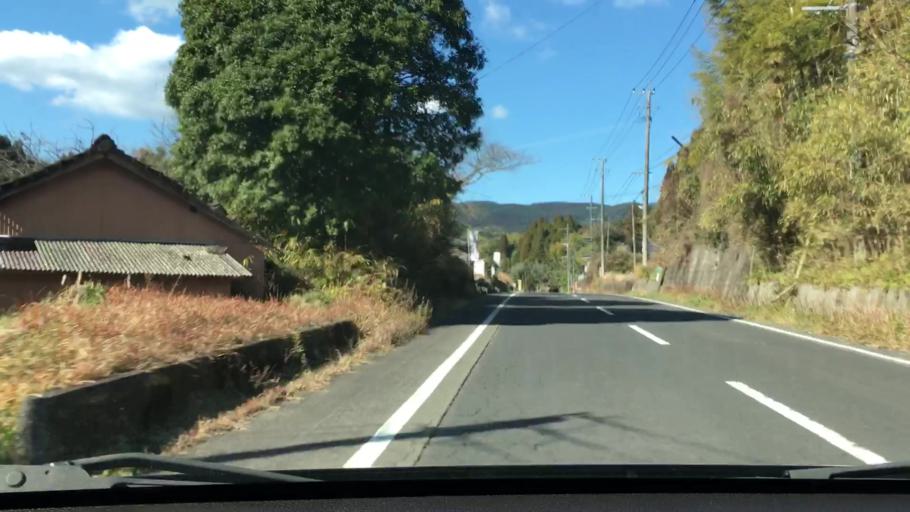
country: JP
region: Kagoshima
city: Ijuin
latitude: 31.7044
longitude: 130.4469
